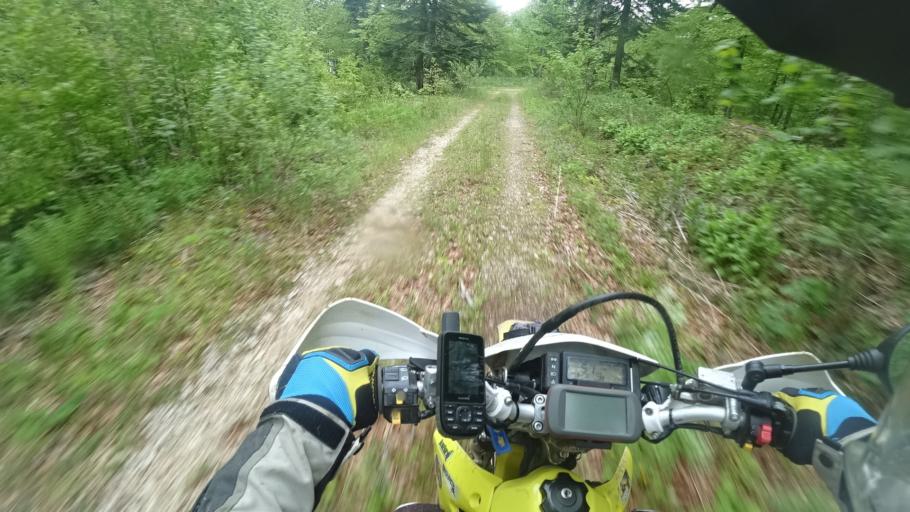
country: BA
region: Federation of Bosnia and Herzegovina
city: Orasac
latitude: 44.5658
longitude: 15.8831
